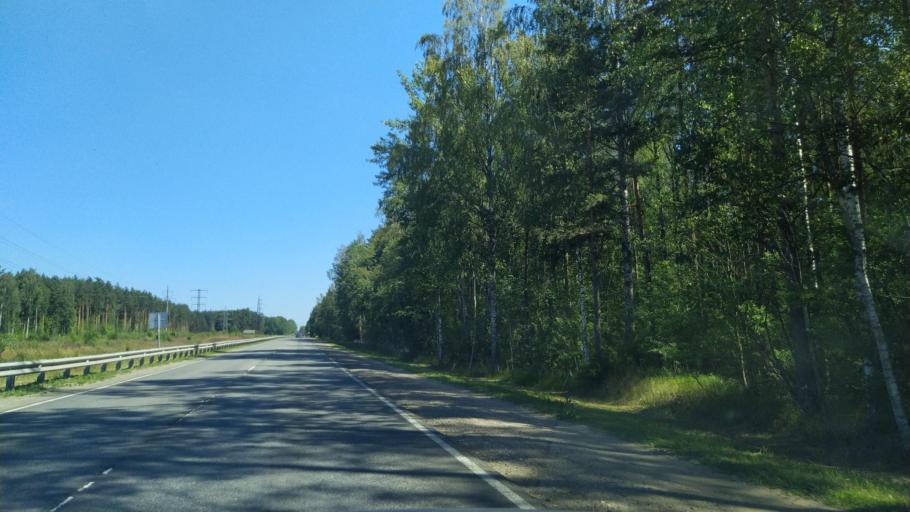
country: RU
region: Leningrad
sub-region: Volosovskiy Rayon
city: Shlissel'burg
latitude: 59.9578
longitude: 31.0015
